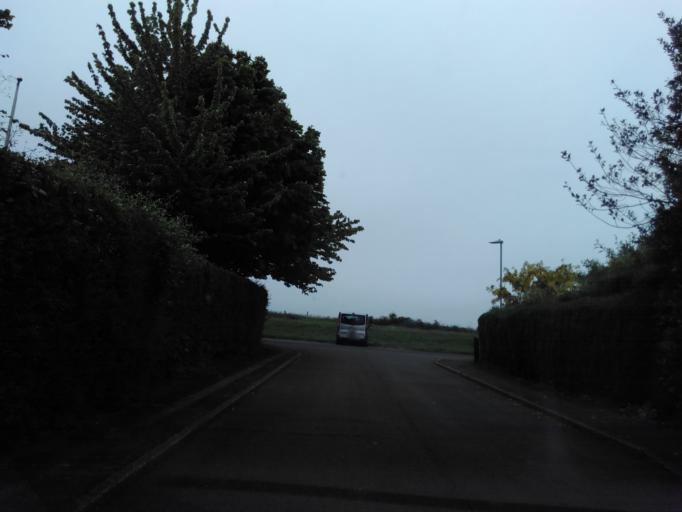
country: GB
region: England
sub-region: Kent
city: Chartham
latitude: 51.2506
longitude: 1.0134
